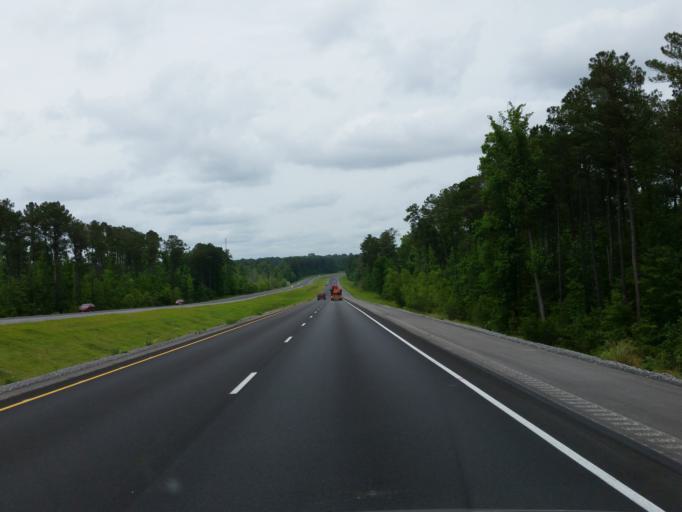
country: US
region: Mississippi
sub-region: Jones County
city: Sharon
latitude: 31.8626
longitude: -89.0466
